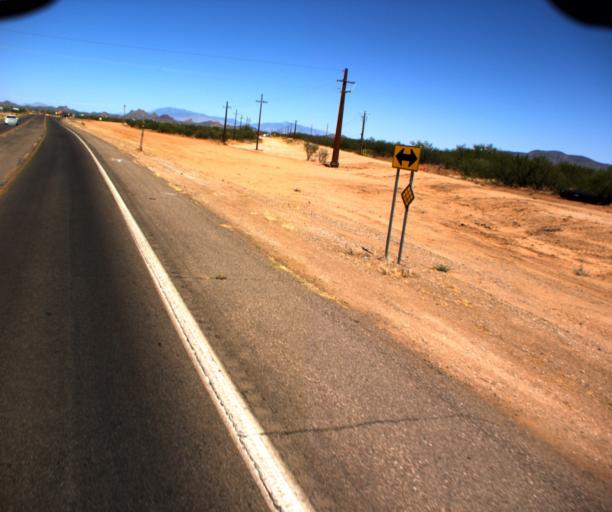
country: US
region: Arizona
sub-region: Pima County
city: Valencia West
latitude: 32.1333
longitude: -111.1736
